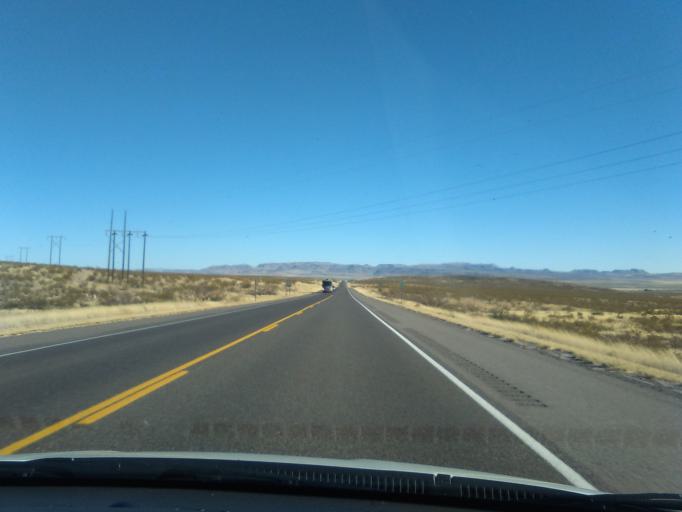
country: US
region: New Mexico
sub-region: Dona Ana County
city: Hatch
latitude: 32.5763
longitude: -107.4306
